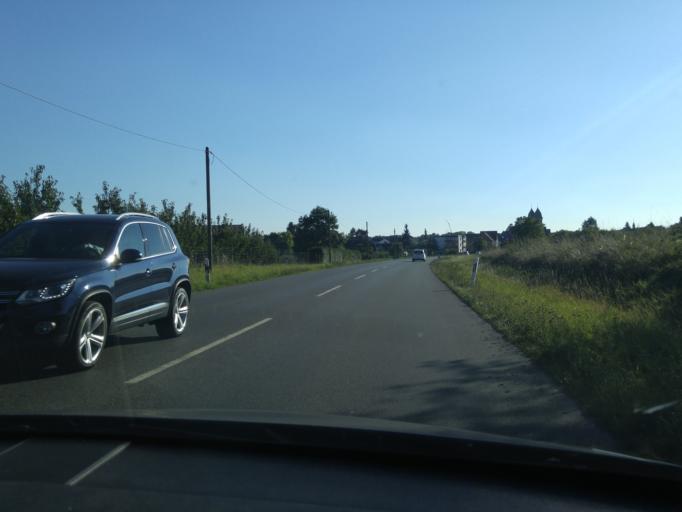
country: DE
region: Hesse
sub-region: Regierungsbezirk Darmstadt
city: Bad Nauheim
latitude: 50.3383
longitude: 8.7246
